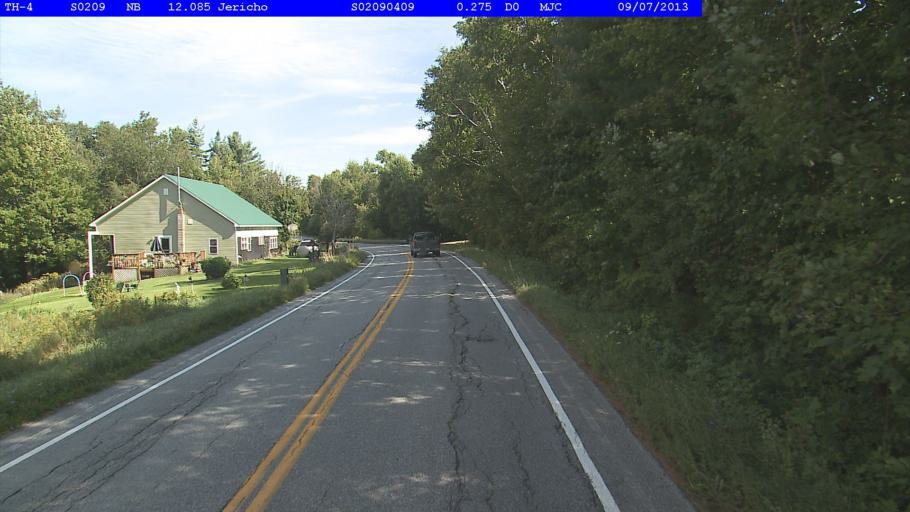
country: US
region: Vermont
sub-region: Chittenden County
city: Jericho
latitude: 44.4353
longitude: -72.9797
